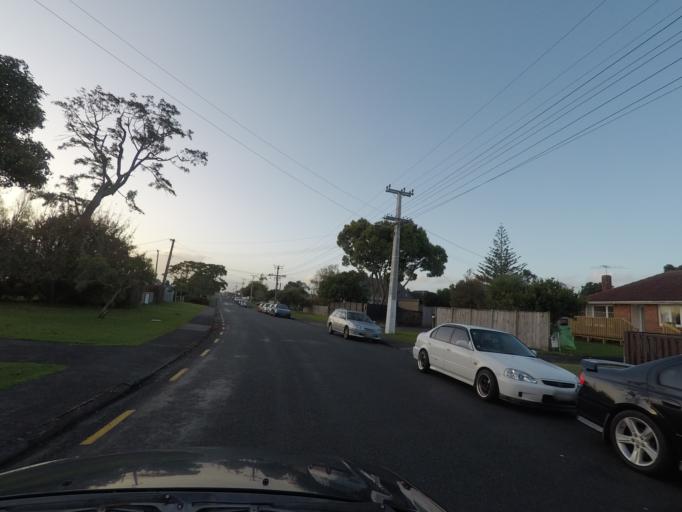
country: NZ
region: Auckland
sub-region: Auckland
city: Rosebank
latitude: -36.8391
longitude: 174.6467
